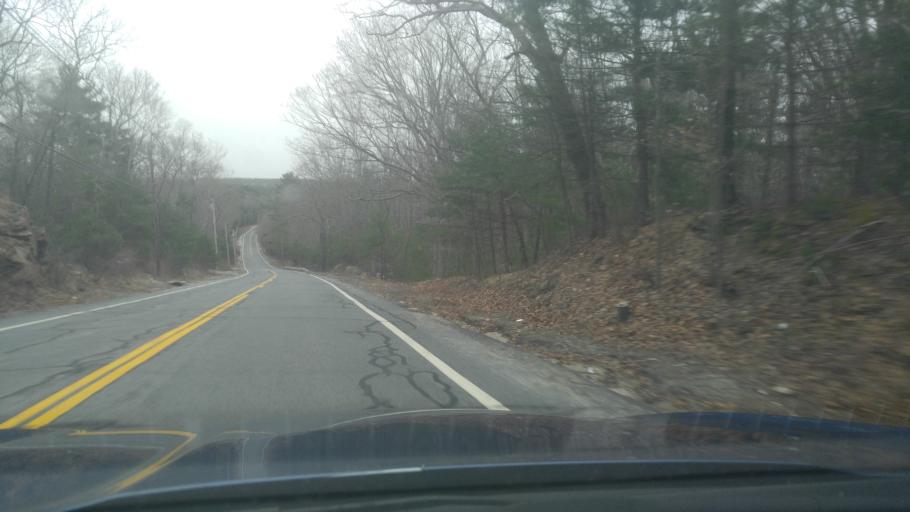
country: US
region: Rhode Island
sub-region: Kent County
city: West Greenwich
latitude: 41.6746
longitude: -71.6445
